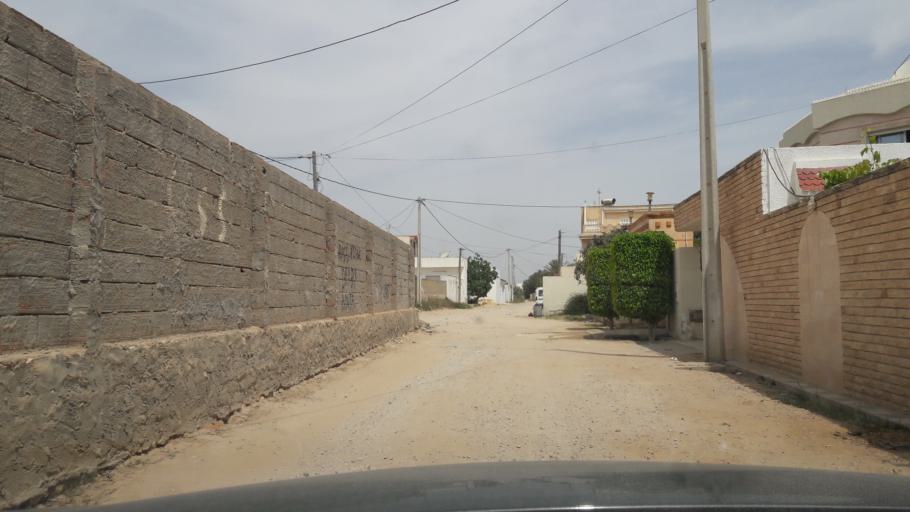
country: TN
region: Safaqis
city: Al Qarmadah
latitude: 34.7834
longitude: 10.7567
